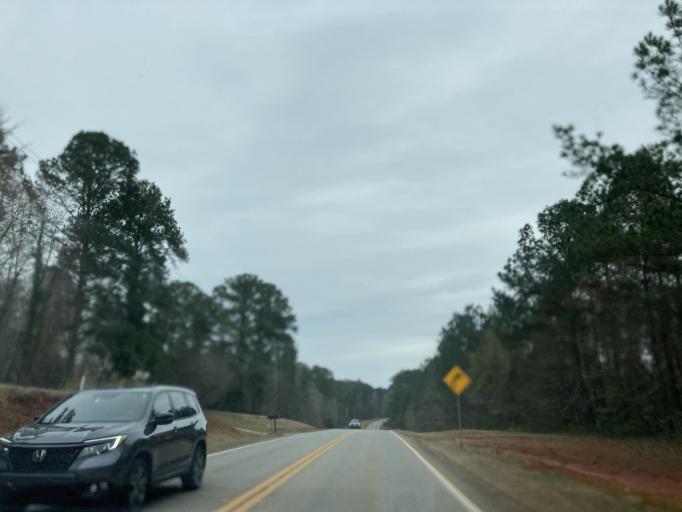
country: US
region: Georgia
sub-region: Jones County
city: Gray
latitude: 32.9917
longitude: -83.5957
